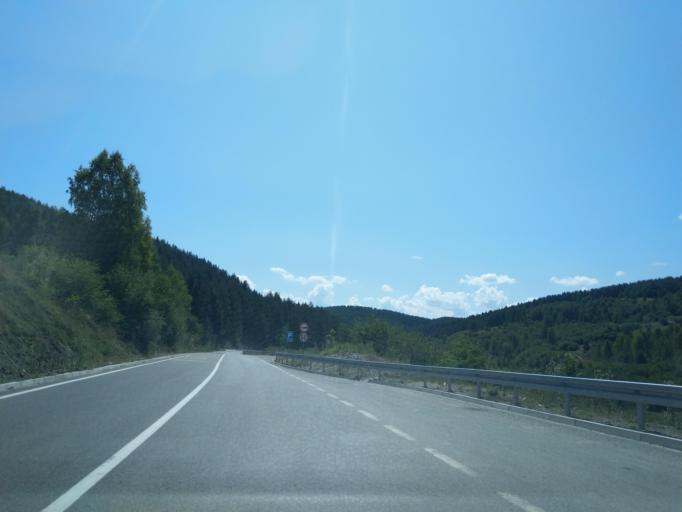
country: RS
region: Central Serbia
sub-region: Zlatiborski Okrug
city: Sjenica
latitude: 43.2865
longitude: 19.9443
